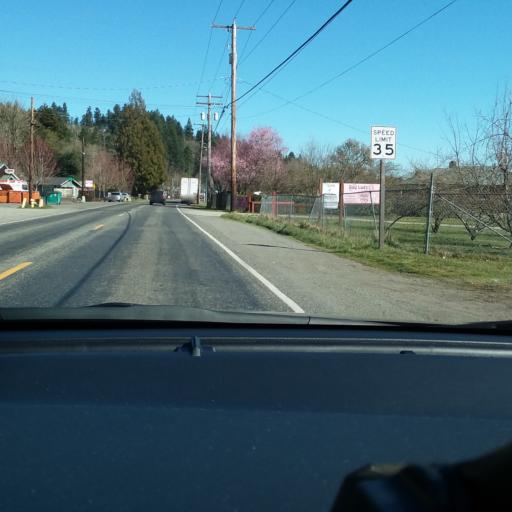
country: US
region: Washington
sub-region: Pierce County
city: North Puyallup
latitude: 47.2069
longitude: -122.2816
